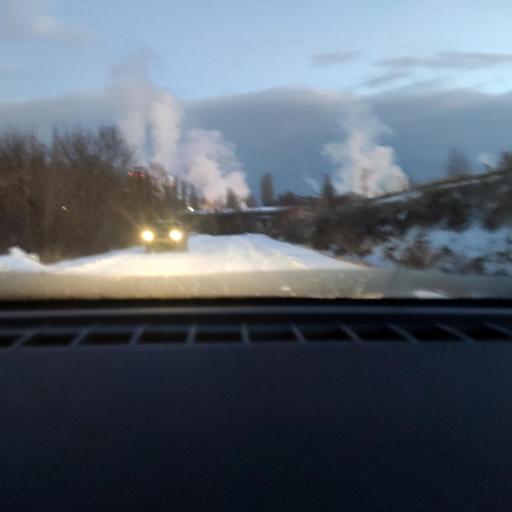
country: RU
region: Voronezj
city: Voronezh
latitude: 51.6204
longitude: 39.2274
